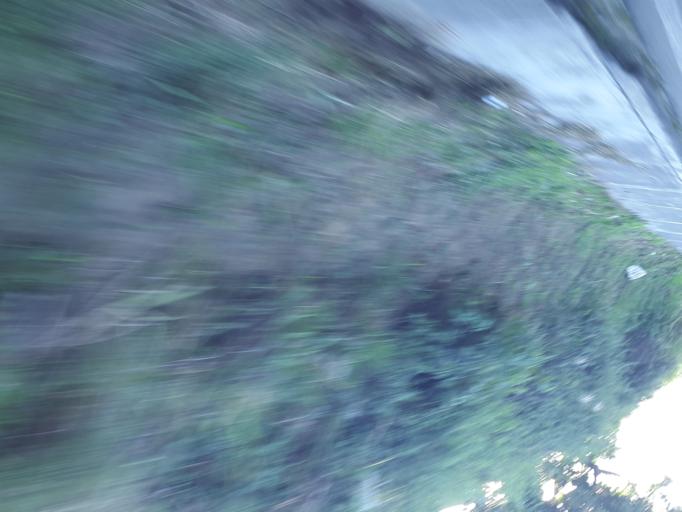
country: CO
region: Quindio
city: Armenia
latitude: 4.5311
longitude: -75.7051
